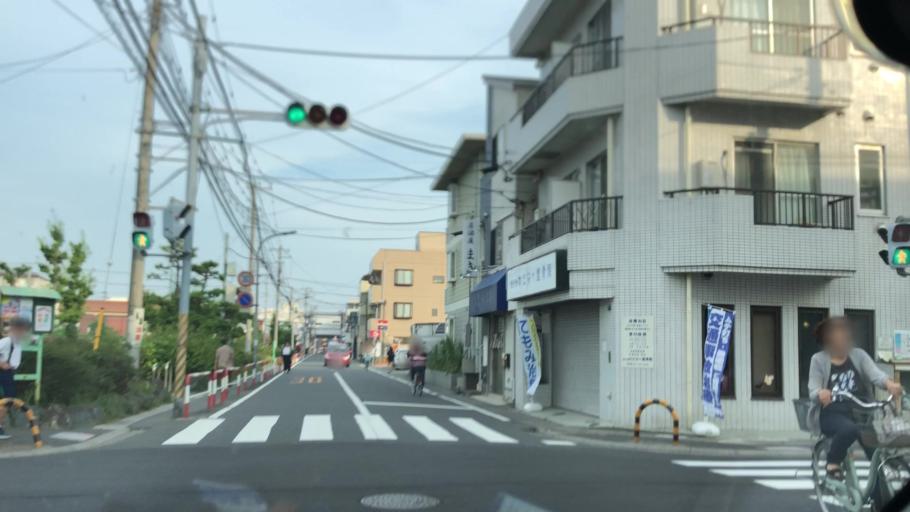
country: JP
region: Tokyo
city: Urayasu
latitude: 35.6751
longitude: 139.9005
